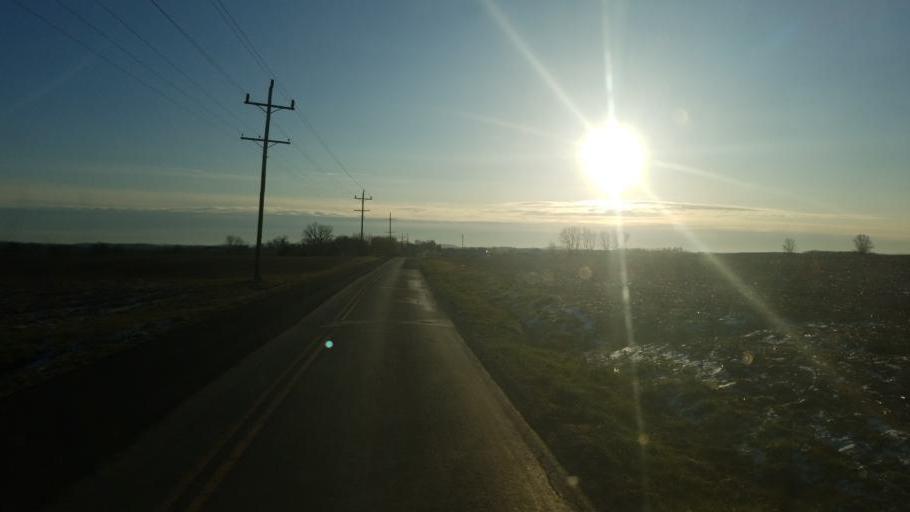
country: US
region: Ohio
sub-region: Highland County
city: Greenfield
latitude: 39.2589
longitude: -83.4595
